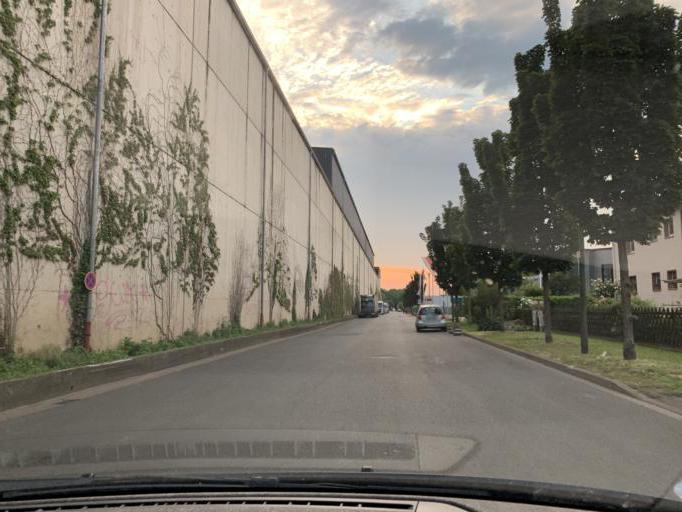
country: DE
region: North Rhine-Westphalia
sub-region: Regierungsbezirk Dusseldorf
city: Dusseldorf
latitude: 51.2218
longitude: 6.7423
